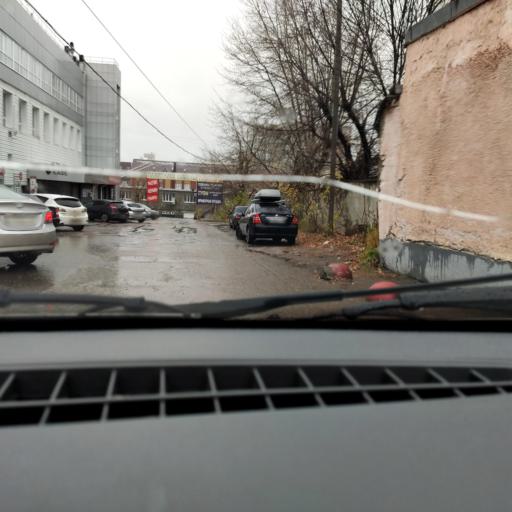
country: RU
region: Bashkortostan
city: Ufa
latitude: 54.7295
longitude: 55.9861
